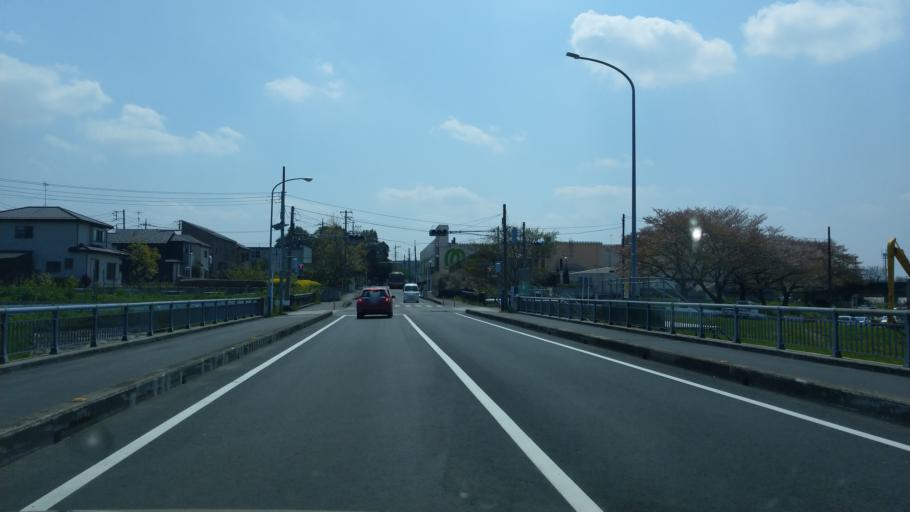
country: JP
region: Saitama
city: Saitama
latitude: 35.8946
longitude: 139.6651
